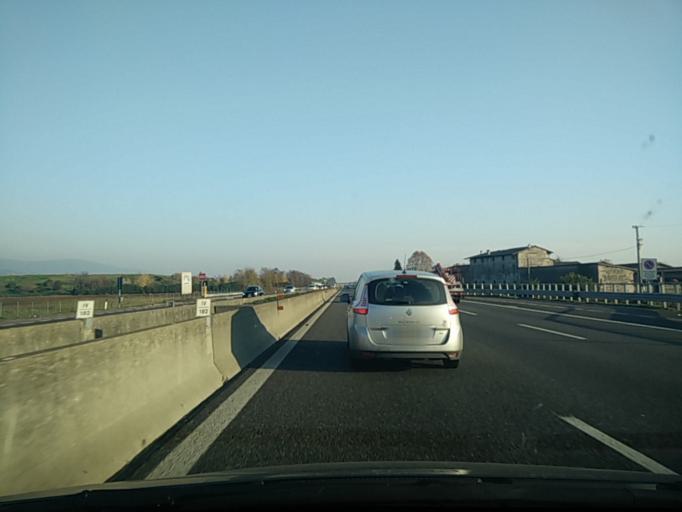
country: IT
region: Lombardy
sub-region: Provincia di Bergamo
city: Bagnatica
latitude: 45.6474
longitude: 9.7897
